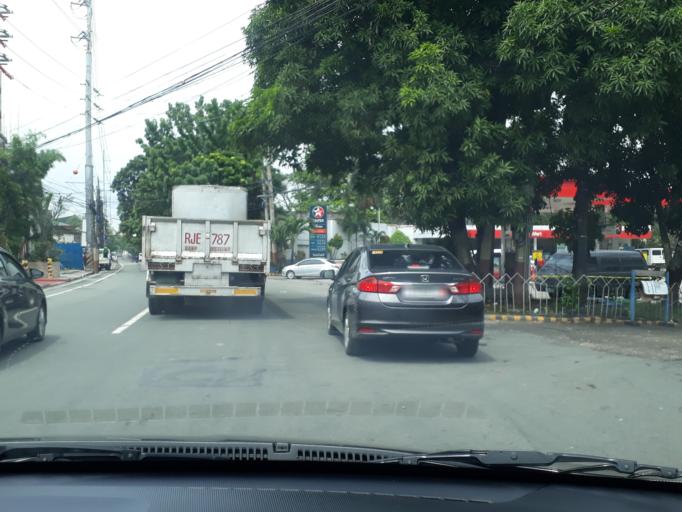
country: PH
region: Metro Manila
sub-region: Marikina
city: Calumpang
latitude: 14.5969
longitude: 121.0897
